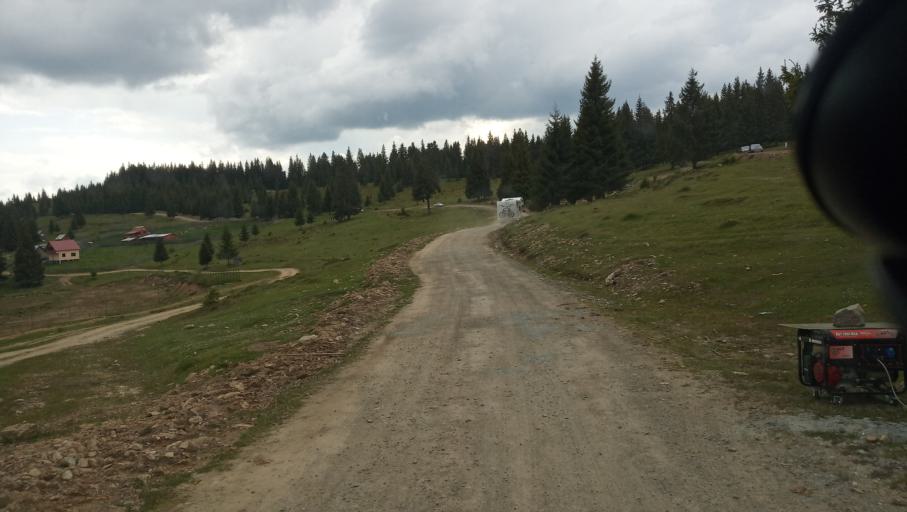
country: RO
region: Cluj
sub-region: Comuna Belis
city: Belis
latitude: 46.6366
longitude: 23.0452
